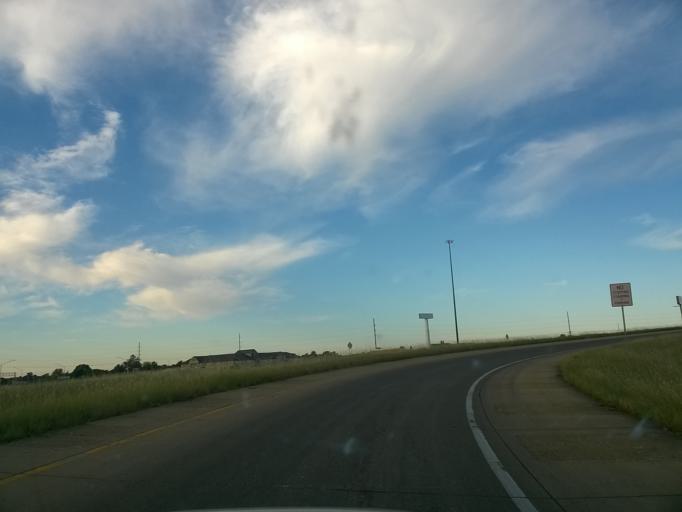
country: US
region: Indiana
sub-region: Warrick County
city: Newburgh
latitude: 37.9755
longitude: -87.4505
